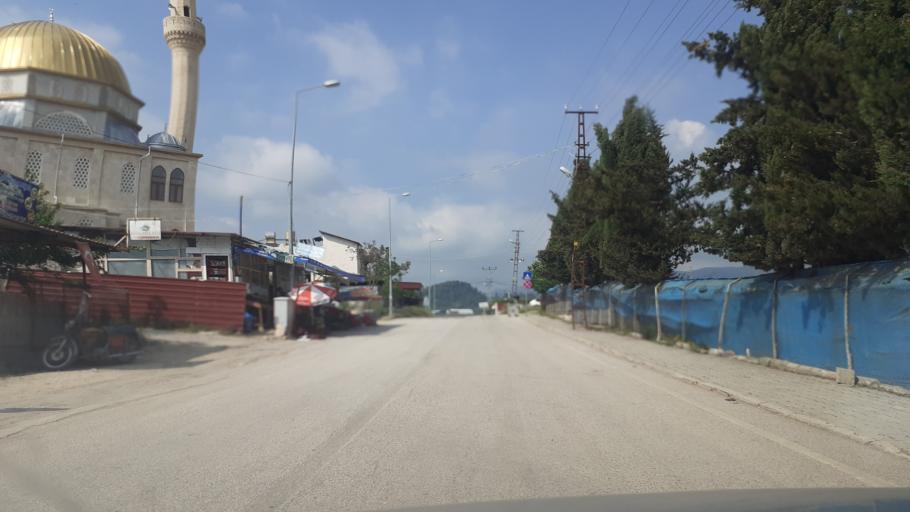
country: TR
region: Hatay
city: Yayladagi
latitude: 35.9081
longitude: 36.0528
